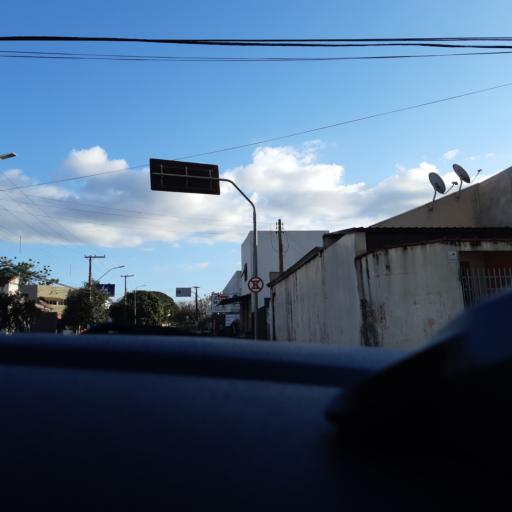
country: BR
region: Sao Paulo
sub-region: Ourinhos
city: Ourinhos
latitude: -22.9839
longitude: -49.8573
